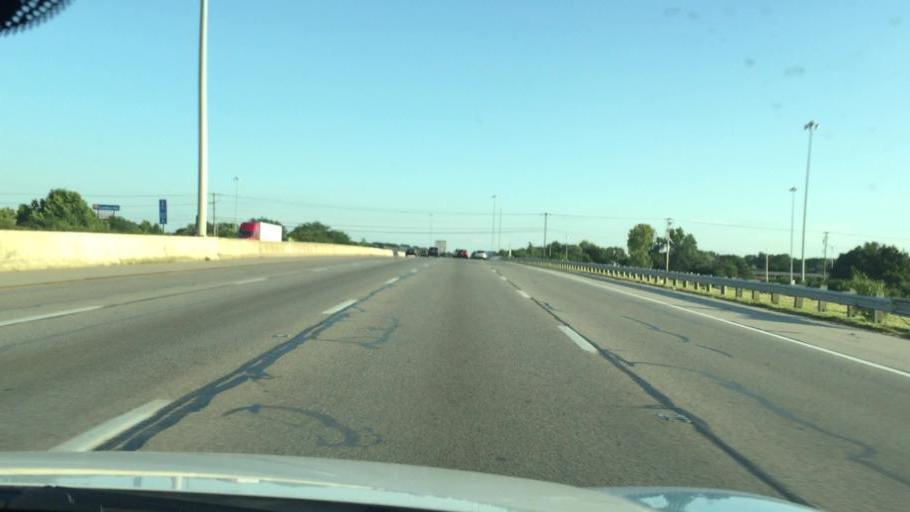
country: US
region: Ohio
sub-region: Franklin County
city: Worthington
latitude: 40.0896
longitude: -82.9873
